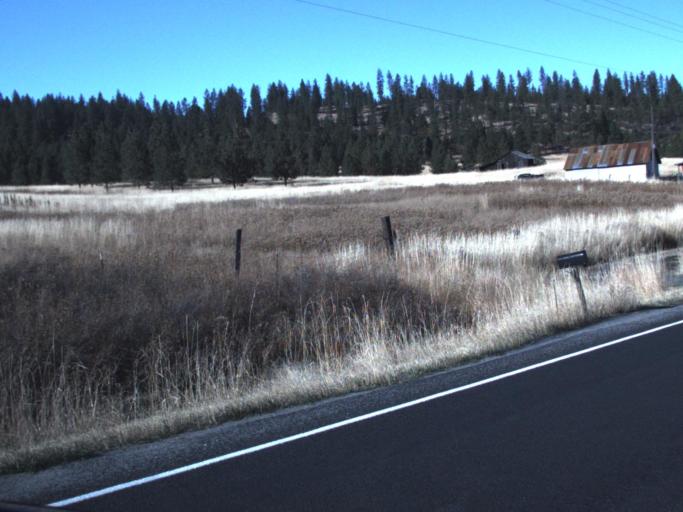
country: US
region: Washington
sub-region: Lincoln County
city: Davenport
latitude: 47.9909
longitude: -118.2874
